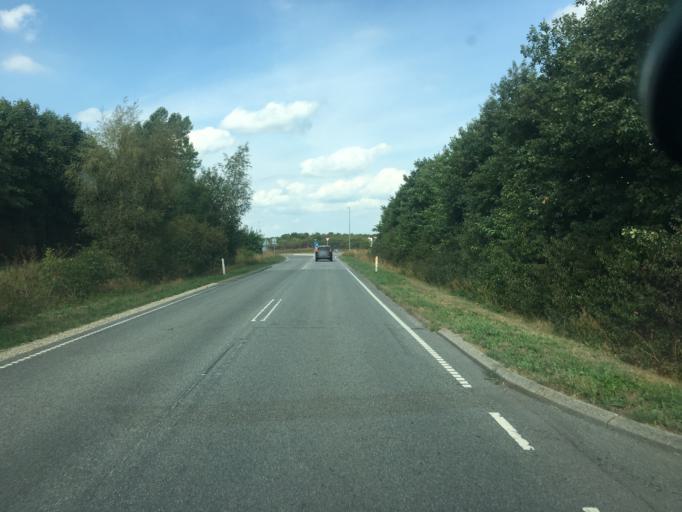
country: DK
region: South Denmark
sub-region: Aabenraa Kommune
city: Tinglev
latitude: 54.9489
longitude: 9.2781
